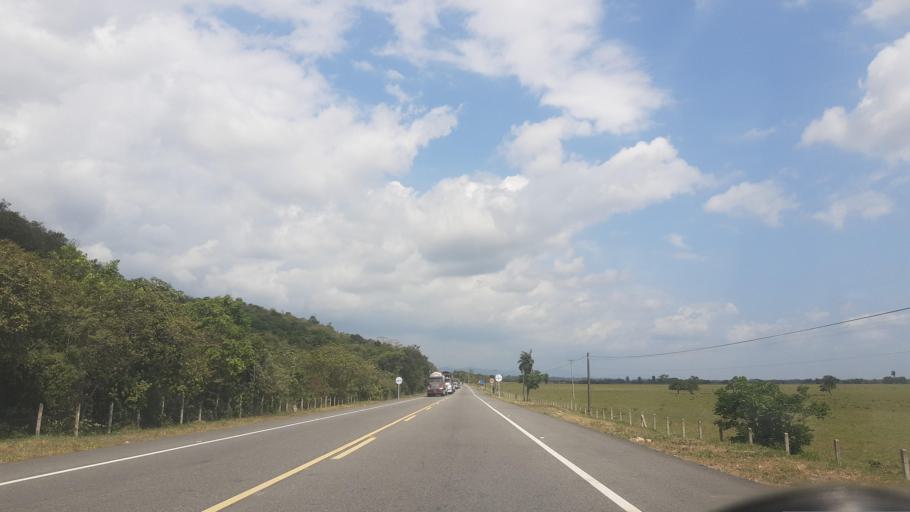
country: CO
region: Casanare
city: Tauramena
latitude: 4.9000
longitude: -72.6766
